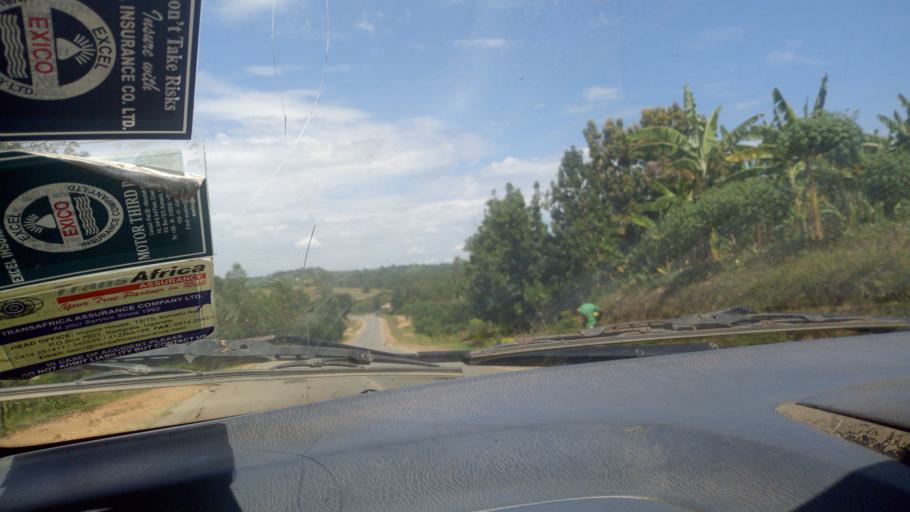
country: UG
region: Western Region
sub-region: Buhweju District
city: Buhweju
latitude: -0.2655
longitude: 30.5602
